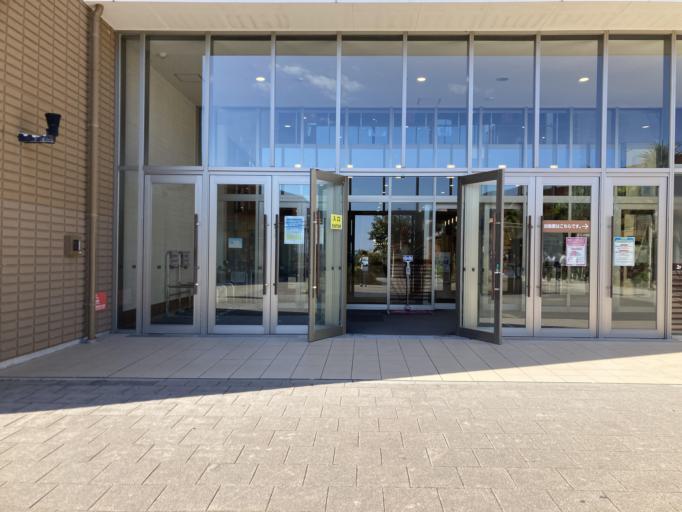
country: JP
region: Okinawa
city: Okinawa
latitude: 26.3144
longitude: 127.7975
